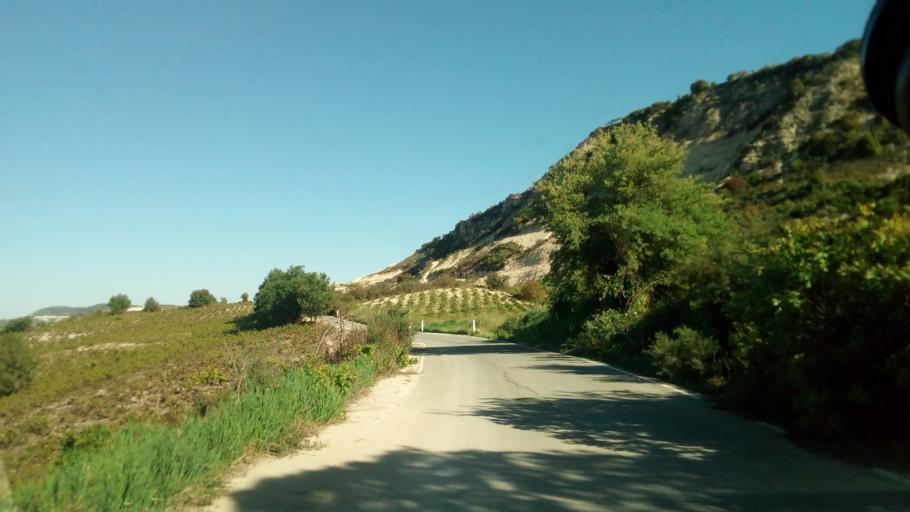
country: CY
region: Limassol
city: Pachna
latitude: 34.8655
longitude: 32.7820
